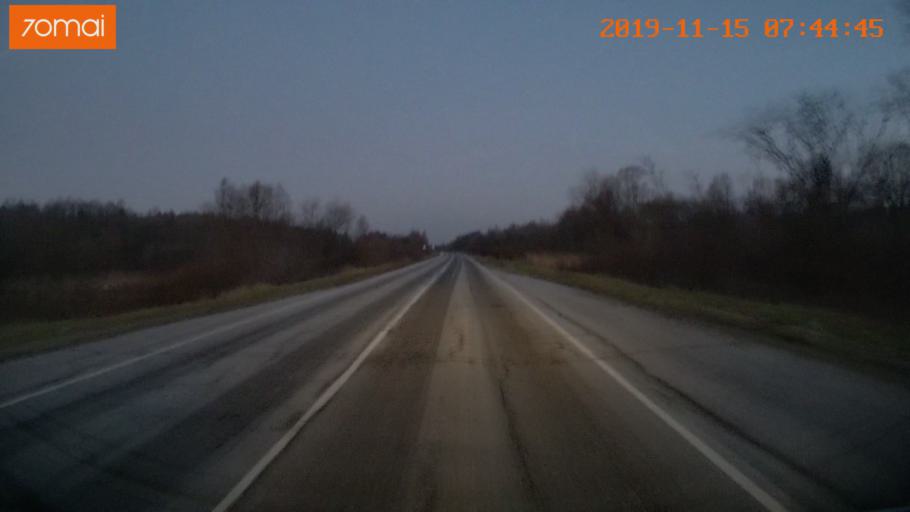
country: RU
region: Vologda
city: Sheksna
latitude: 58.8154
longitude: 38.3103
